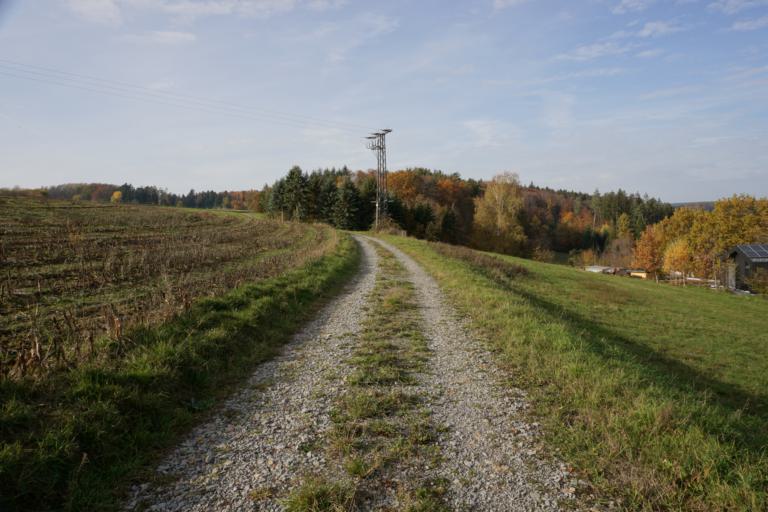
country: DE
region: Baden-Wuerttemberg
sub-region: Karlsruhe Region
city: Limbach
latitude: 49.4278
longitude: 9.2306
